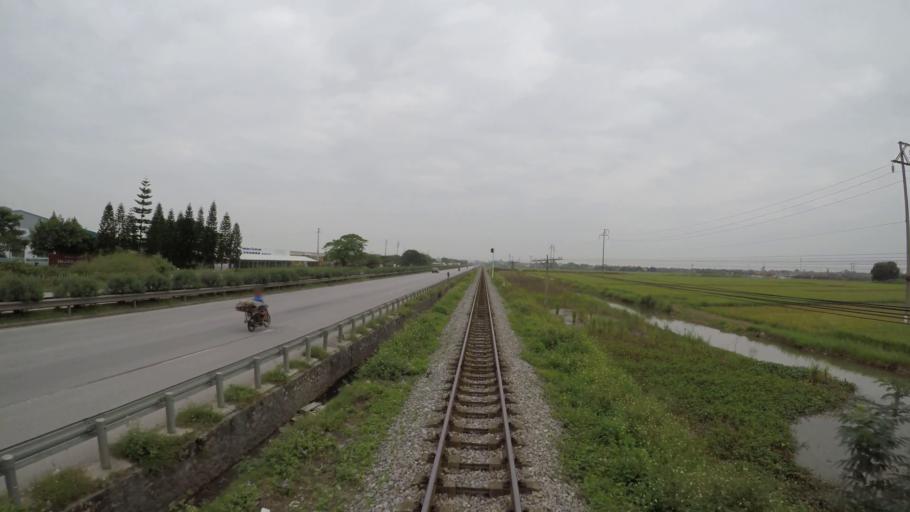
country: VN
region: Hai Duong
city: Phu Thai
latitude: 20.9638
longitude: 106.5167
